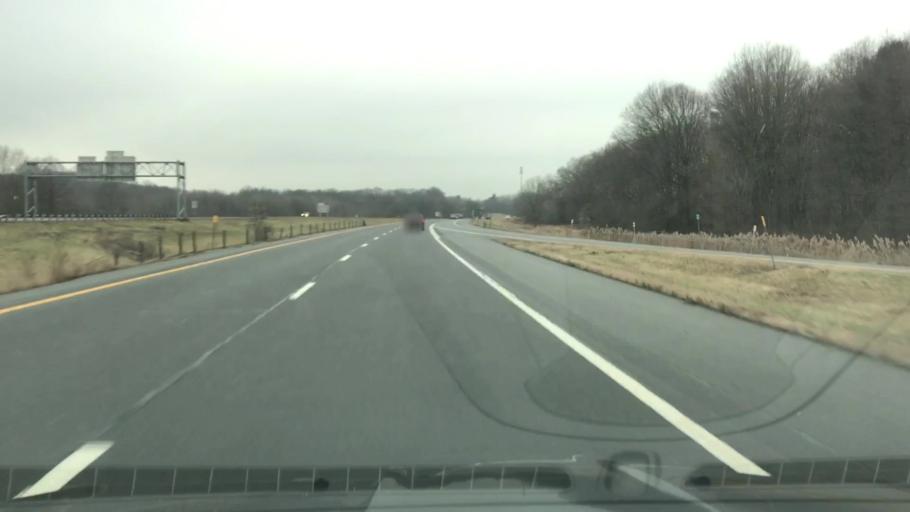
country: US
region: New York
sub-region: Orange County
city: Middletown
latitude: 41.4130
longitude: -74.4292
